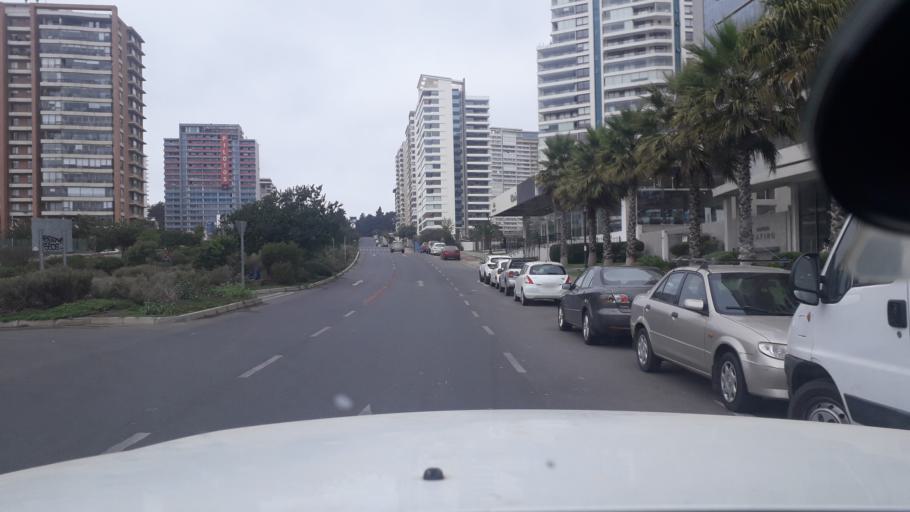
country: CL
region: Valparaiso
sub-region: Provincia de Valparaiso
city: Vina del Mar
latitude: -32.9491
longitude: -71.5440
